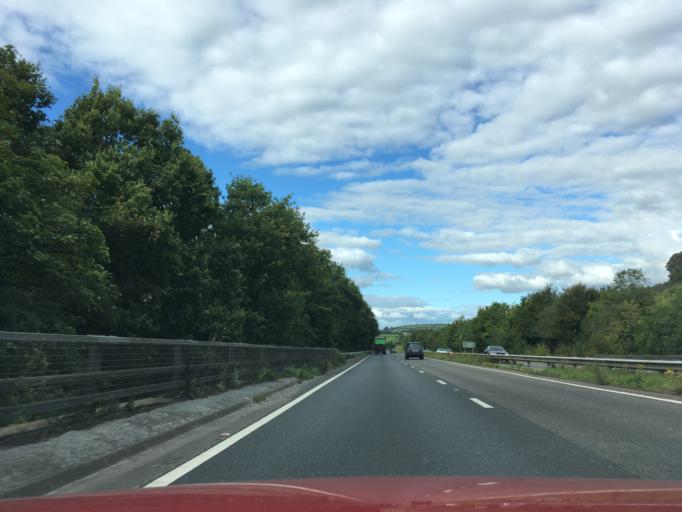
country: GB
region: England
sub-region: Devon
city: Buckfastleigh
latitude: 50.4721
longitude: -3.7865
